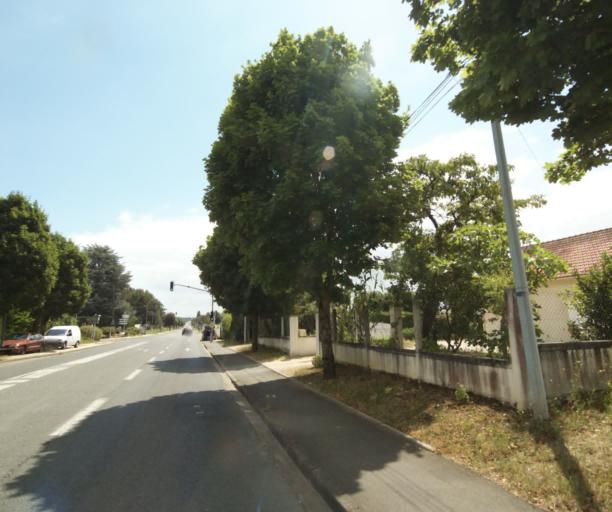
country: FR
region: Centre
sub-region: Departement du Loiret
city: Checy
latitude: 47.9010
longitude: 2.0080
